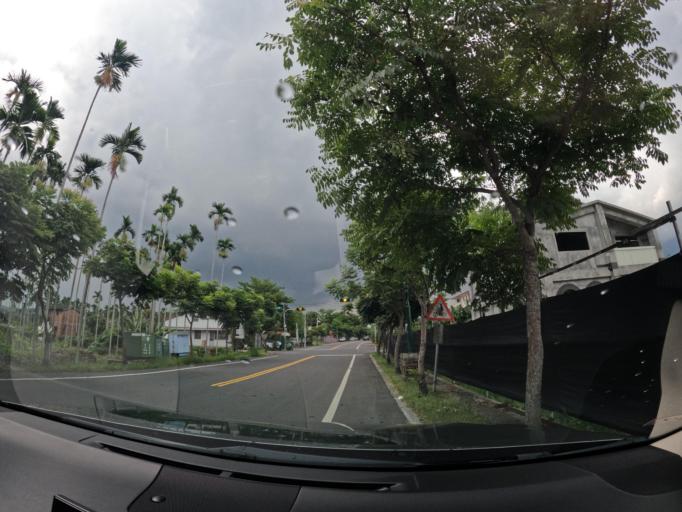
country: TW
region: Taiwan
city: Lugu
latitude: 23.8249
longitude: 120.7927
